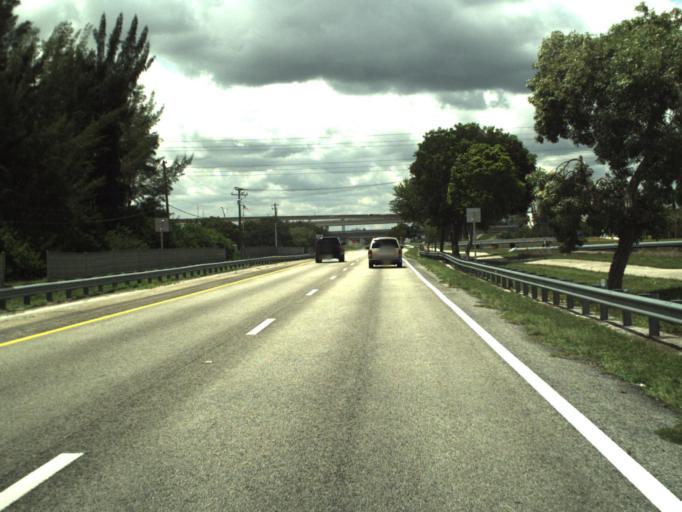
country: US
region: Florida
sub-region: Broward County
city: Southwest Ranches
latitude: 26.1207
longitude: -80.3375
